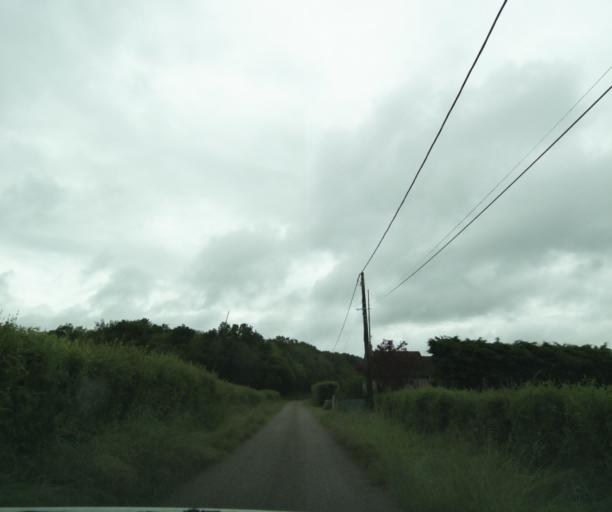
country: FR
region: Bourgogne
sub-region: Departement de Saone-et-Loire
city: Charolles
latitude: 46.5034
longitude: 4.2904
